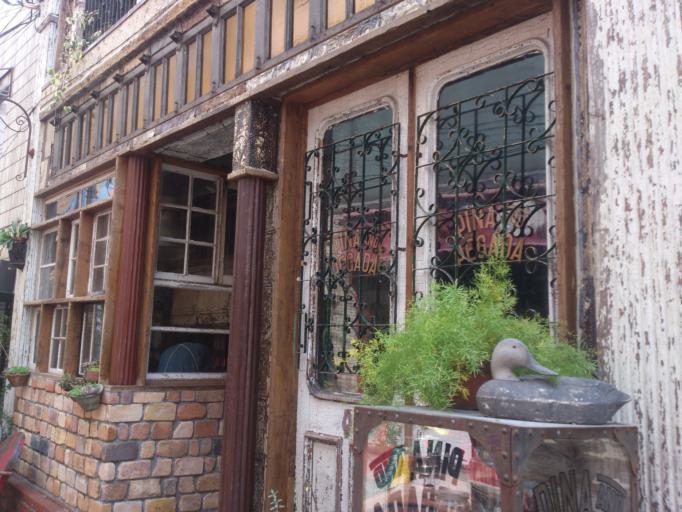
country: JP
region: Kagoshima
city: Kagoshima-shi
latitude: 31.5919
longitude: 130.5539
